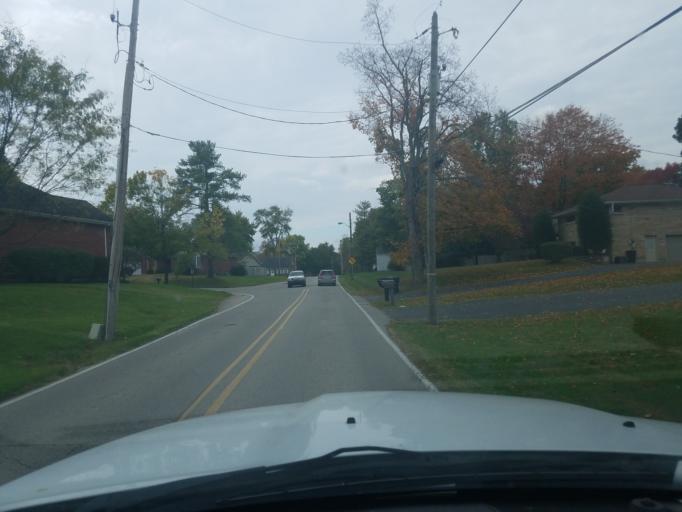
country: US
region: Indiana
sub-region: Floyd County
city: New Albany
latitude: 38.3343
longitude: -85.8039
